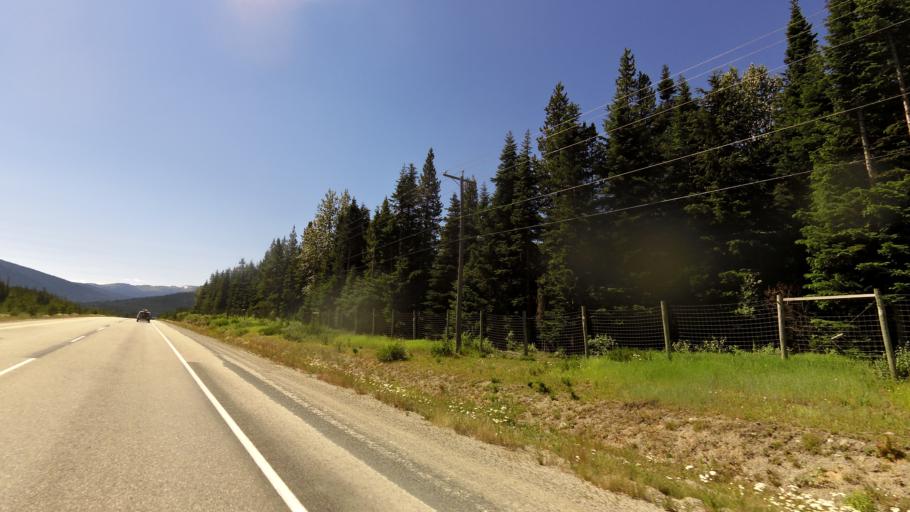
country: CA
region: British Columbia
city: Merritt
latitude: 49.6727
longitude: -121.0150
